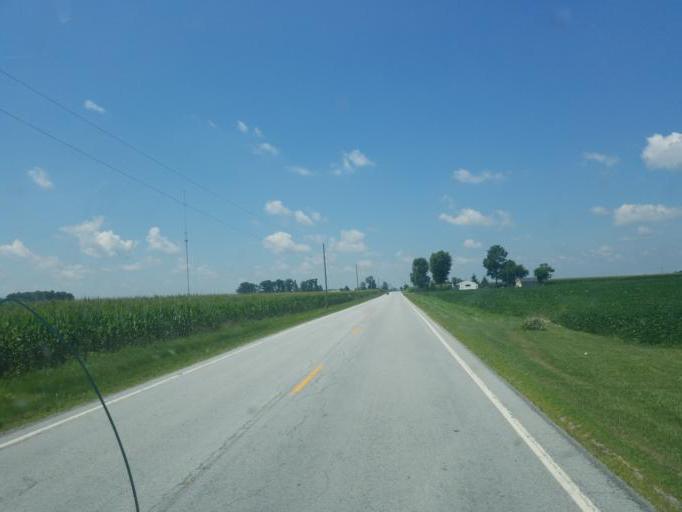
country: US
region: Ohio
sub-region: Allen County
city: Spencerville
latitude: 40.7141
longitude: -84.3748
